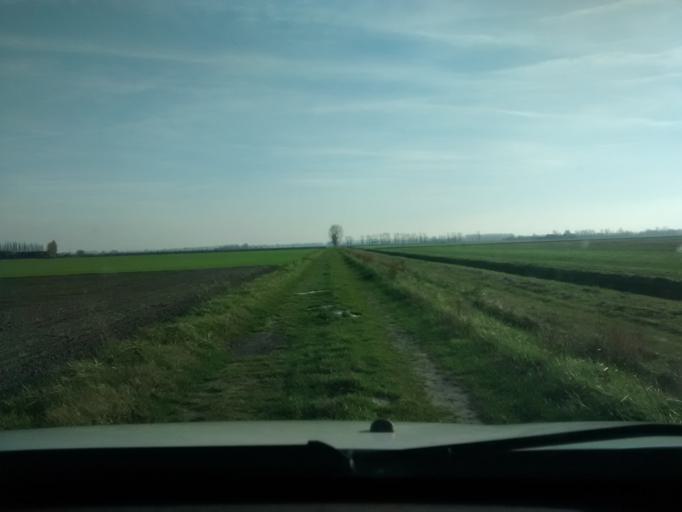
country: FR
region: Brittany
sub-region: Departement d'Ille-et-Vilaine
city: Roz-sur-Couesnon
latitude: 48.6118
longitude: -1.5917
